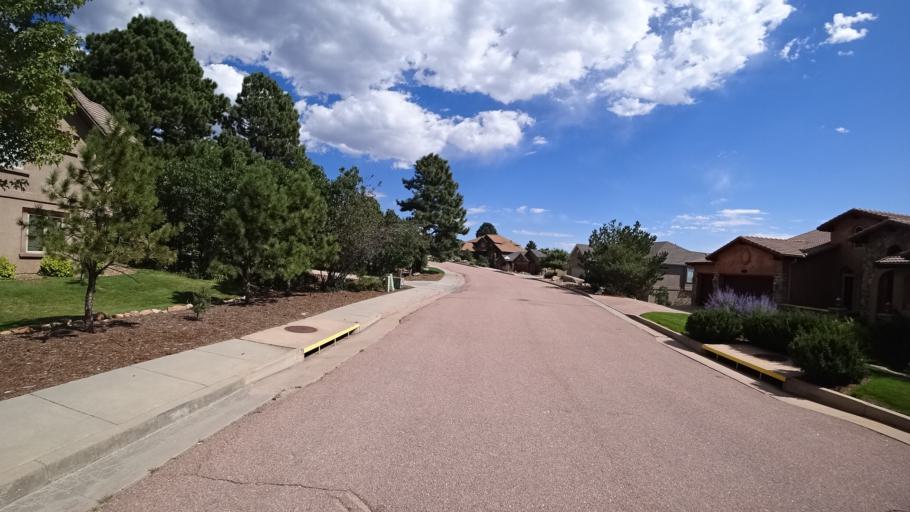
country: US
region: Colorado
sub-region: El Paso County
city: Fort Carson
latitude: 38.7503
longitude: -104.8373
